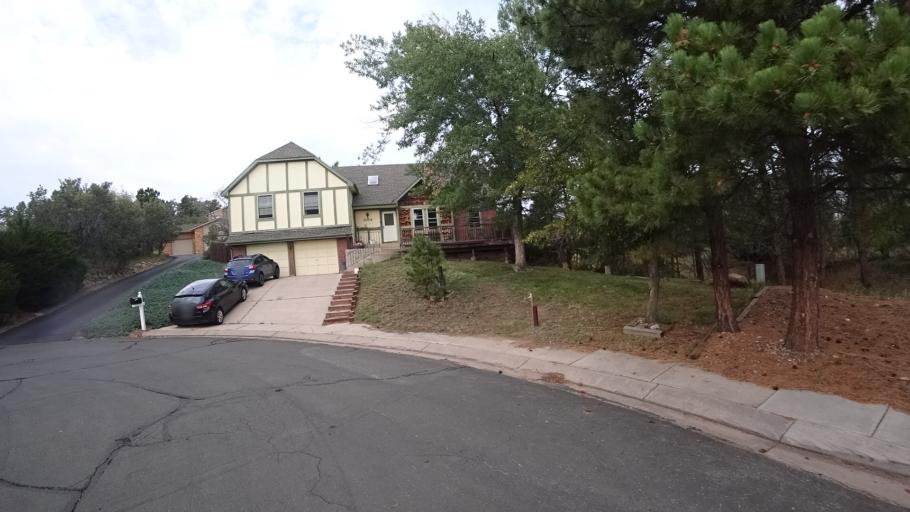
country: US
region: Colorado
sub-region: El Paso County
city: Air Force Academy
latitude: 38.9290
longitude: -104.8488
